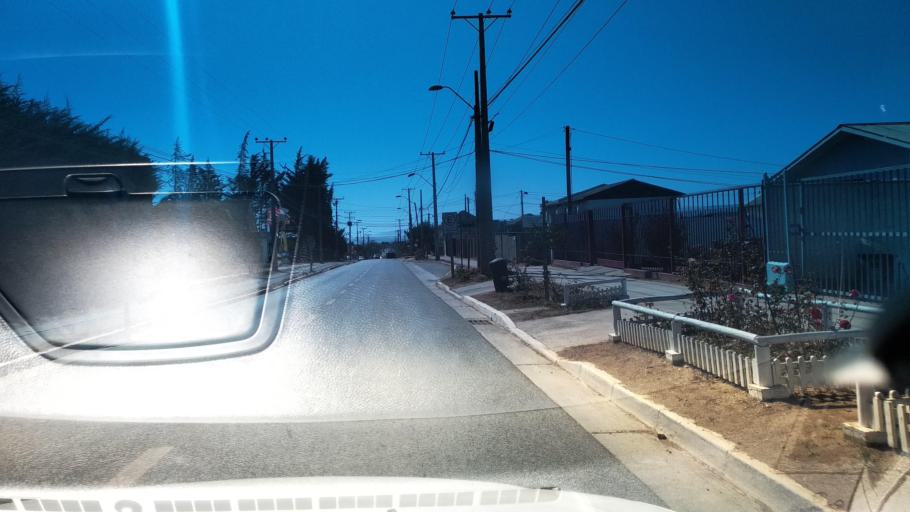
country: CL
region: O'Higgins
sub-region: Provincia de Colchagua
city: Santa Cruz
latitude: -34.3998
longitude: -71.9956
